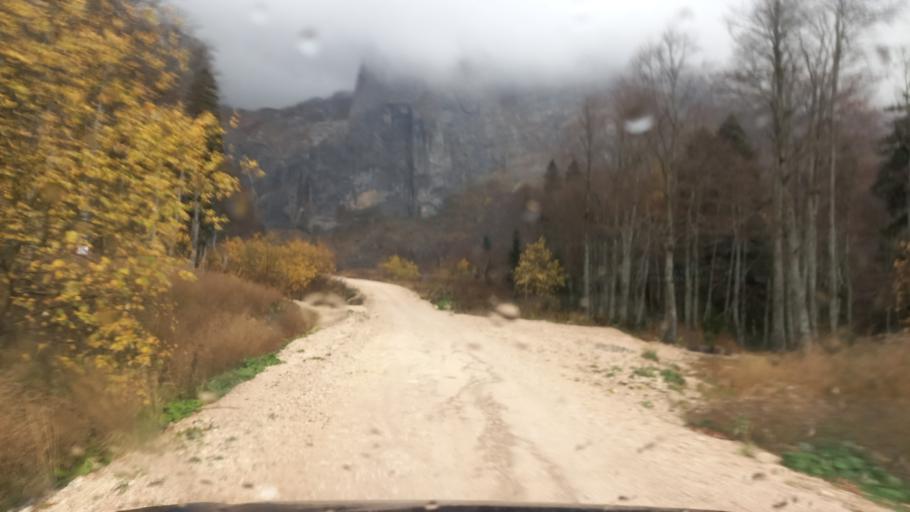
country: RU
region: Krasnodarskiy
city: Dagomys
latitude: 43.9796
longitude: 39.8671
